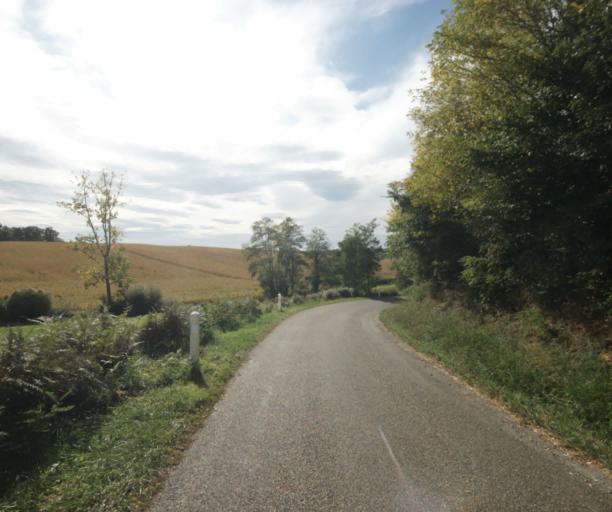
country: FR
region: Midi-Pyrenees
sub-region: Departement du Gers
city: Cazaubon
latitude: 43.8999
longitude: -0.1600
